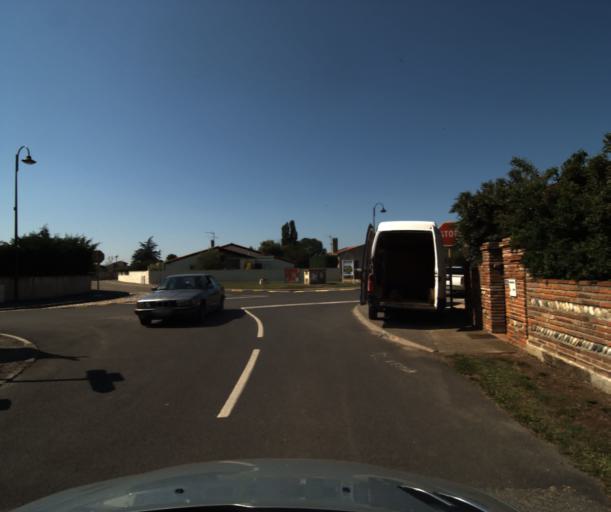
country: FR
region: Midi-Pyrenees
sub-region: Departement de la Haute-Garonne
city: Labarthe-sur-Leze
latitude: 43.4673
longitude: 1.3777
